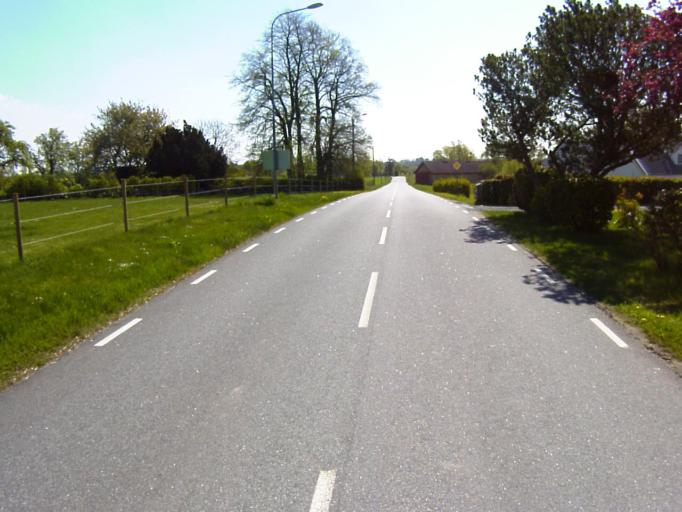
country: SE
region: Skane
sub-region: Kristianstads Kommun
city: Fjalkinge
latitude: 56.0094
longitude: 14.2461
